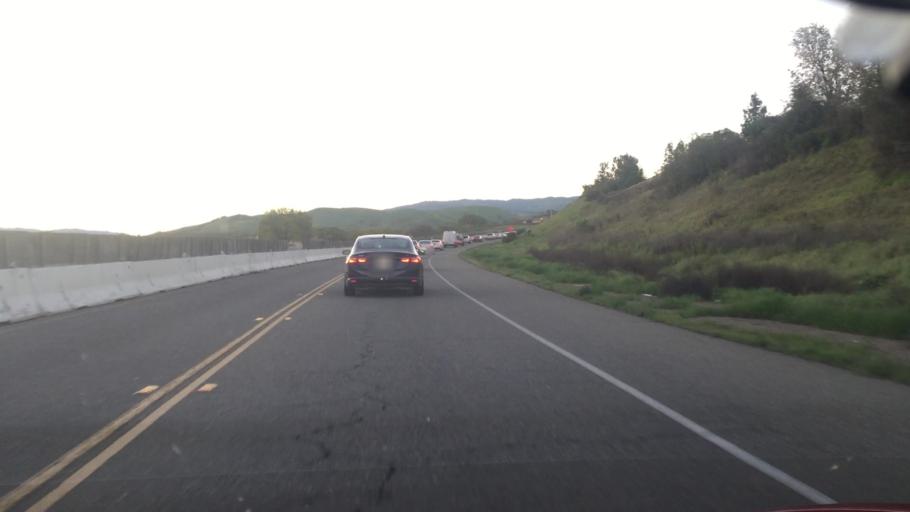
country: US
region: California
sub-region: Alameda County
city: Livermore
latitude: 37.6442
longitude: -121.8009
